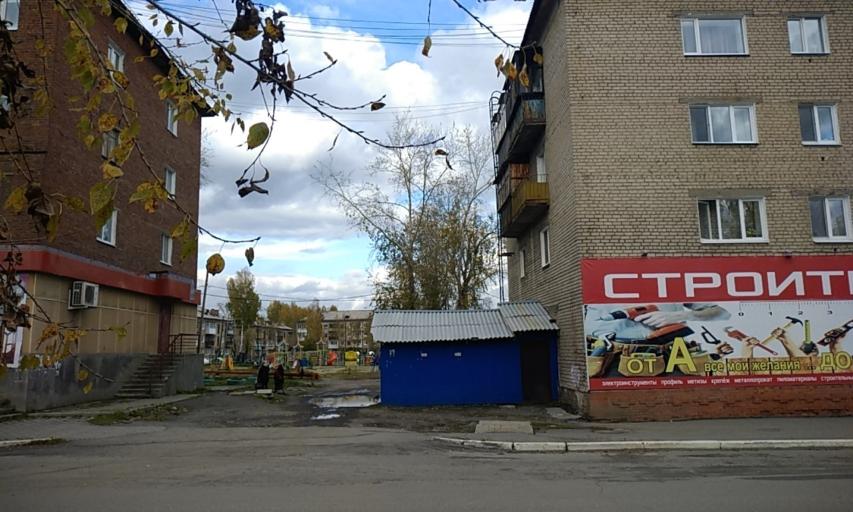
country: RU
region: Sverdlovsk
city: Krasnoural'sk
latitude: 58.3577
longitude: 60.0365
